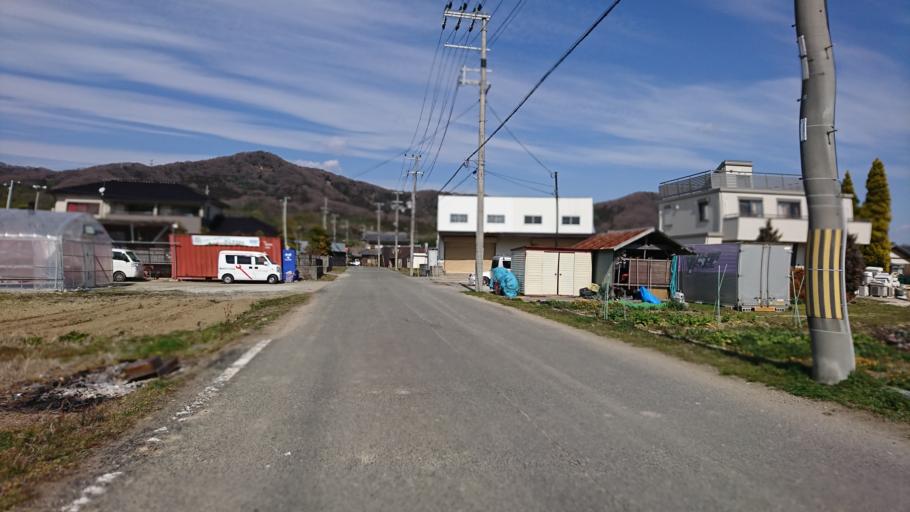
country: JP
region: Hyogo
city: Kakogawacho-honmachi
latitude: 34.8226
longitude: 134.8054
